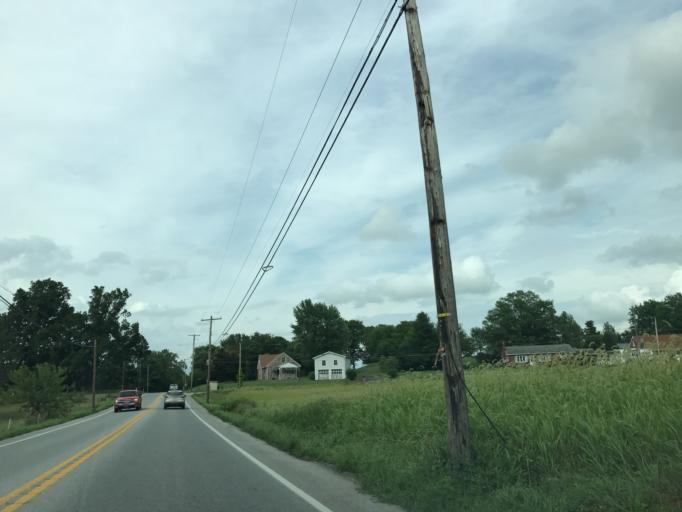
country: US
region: Pennsylvania
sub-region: York County
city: Spring Grove
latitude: 39.8427
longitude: -76.9032
